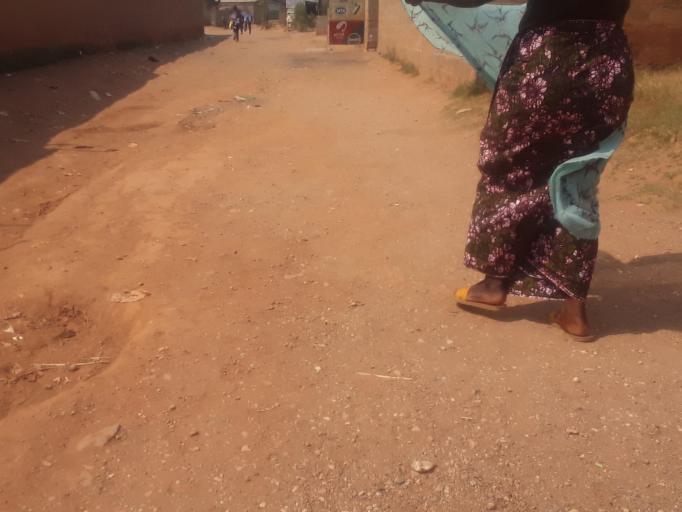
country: ZM
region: Lusaka
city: Lusaka
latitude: -15.3536
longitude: 28.2942
